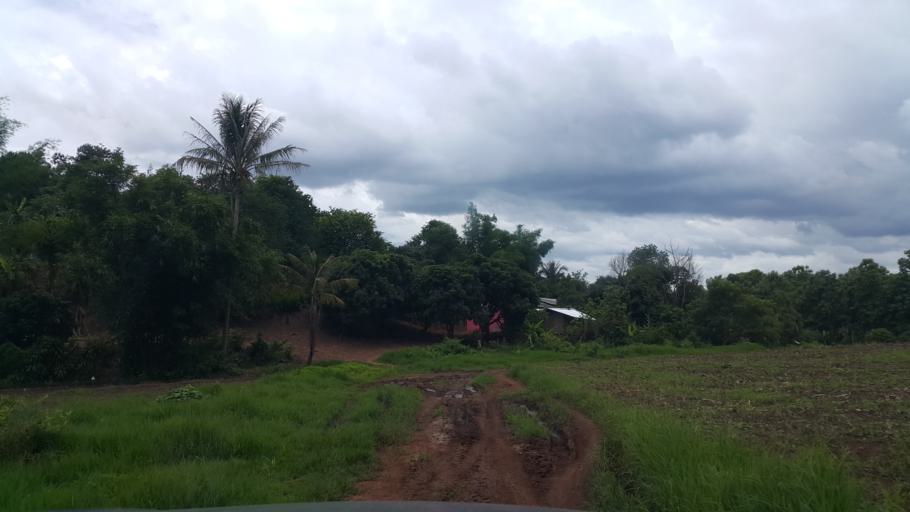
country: TH
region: Chiang Mai
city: Mae Taeng
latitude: 19.2308
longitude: 98.9958
